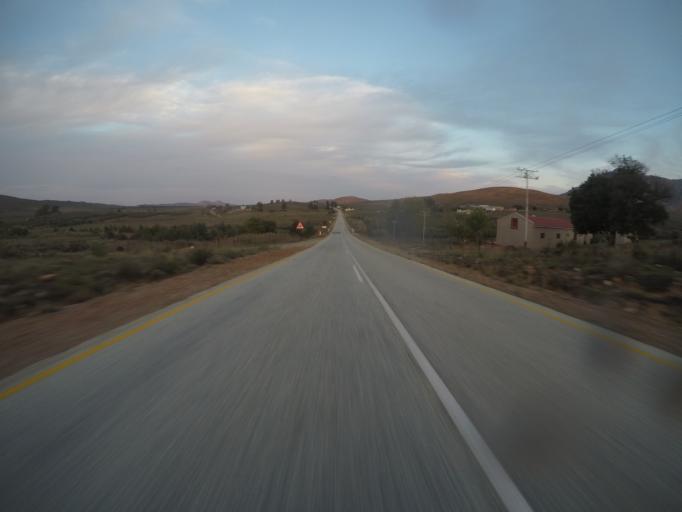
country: ZA
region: Western Cape
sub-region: Eden District Municipality
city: Plettenberg Bay
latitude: -33.7328
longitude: 23.4027
